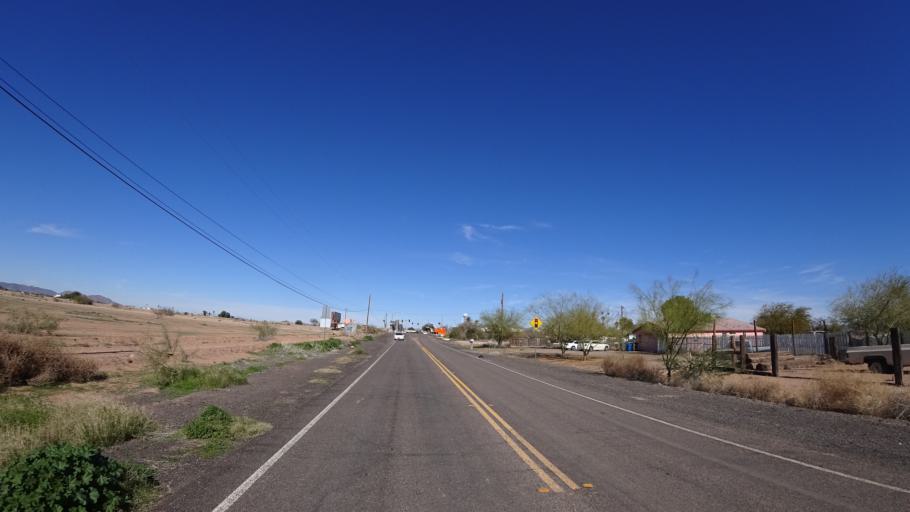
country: US
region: Arizona
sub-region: Maricopa County
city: Scottsdale
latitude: 33.4641
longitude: -111.8661
